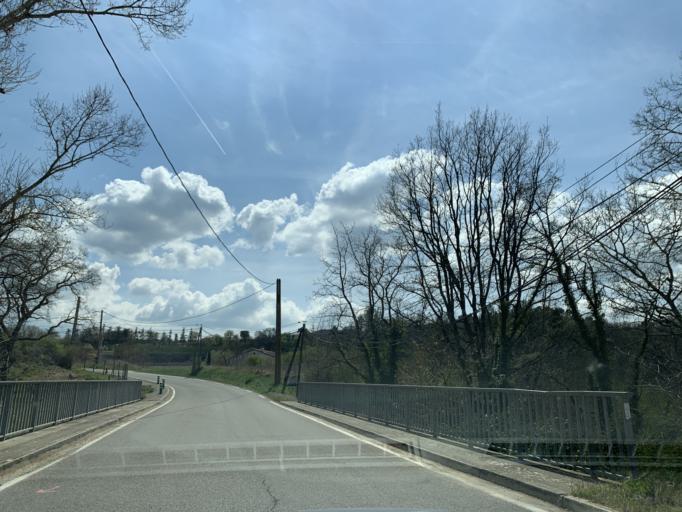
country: FR
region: Provence-Alpes-Cote d'Azur
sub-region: Departement du Vaucluse
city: Goult
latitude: 43.8689
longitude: 5.2464
